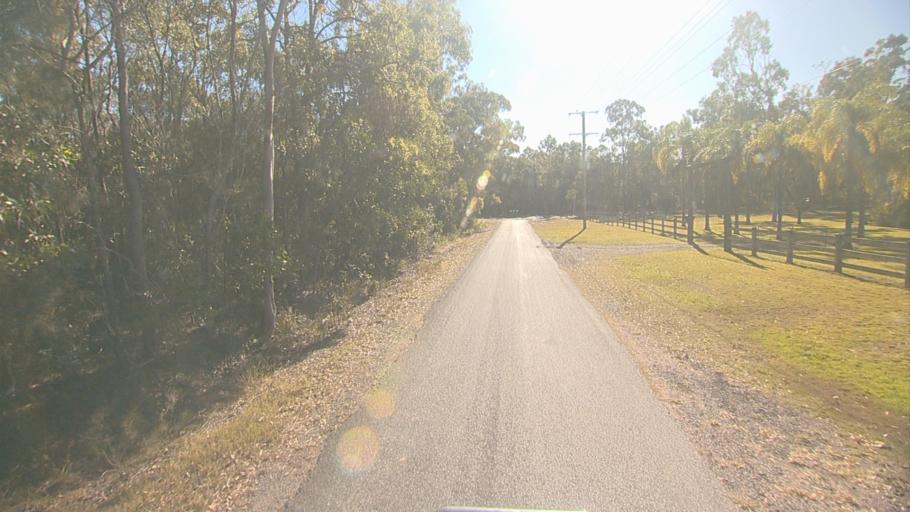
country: AU
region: Queensland
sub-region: Logan
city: Park Ridge South
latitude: -27.7479
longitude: 153.0485
